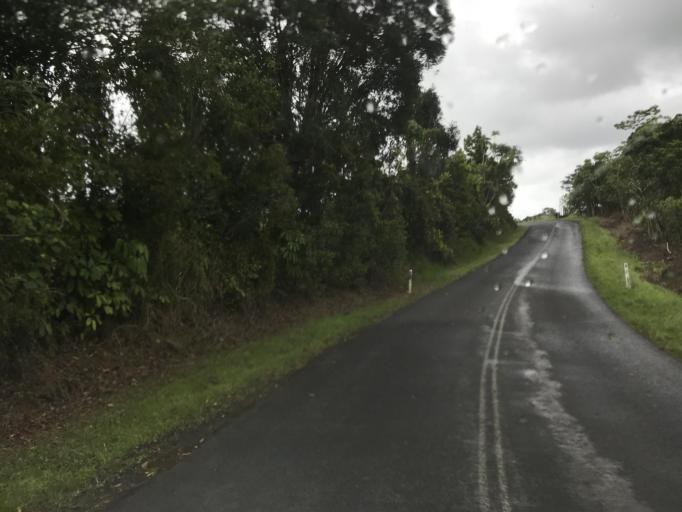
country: AU
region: Queensland
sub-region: Cassowary Coast
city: Innisfail
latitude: -17.5174
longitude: 145.9727
